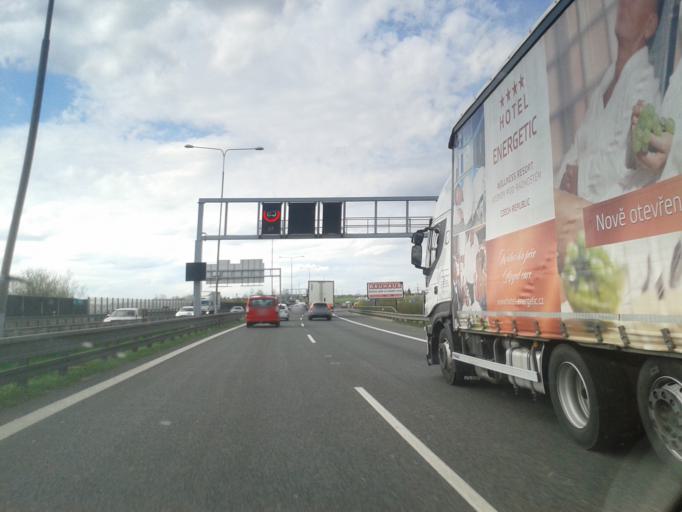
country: CZ
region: Central Bohemia
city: Trebotov
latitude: 50.0269
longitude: 14.2905
